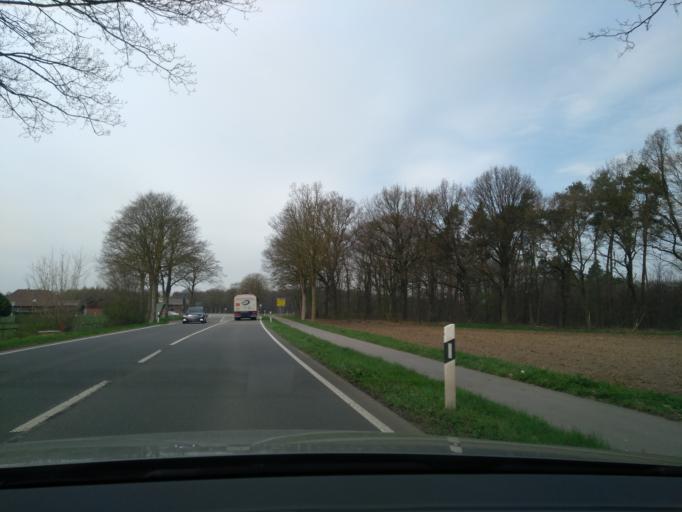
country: DE
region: North Rhine-Westphalia
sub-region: Regierungsbezirk Dusseldorf
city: Issum
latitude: 51.5834
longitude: 6.4337
